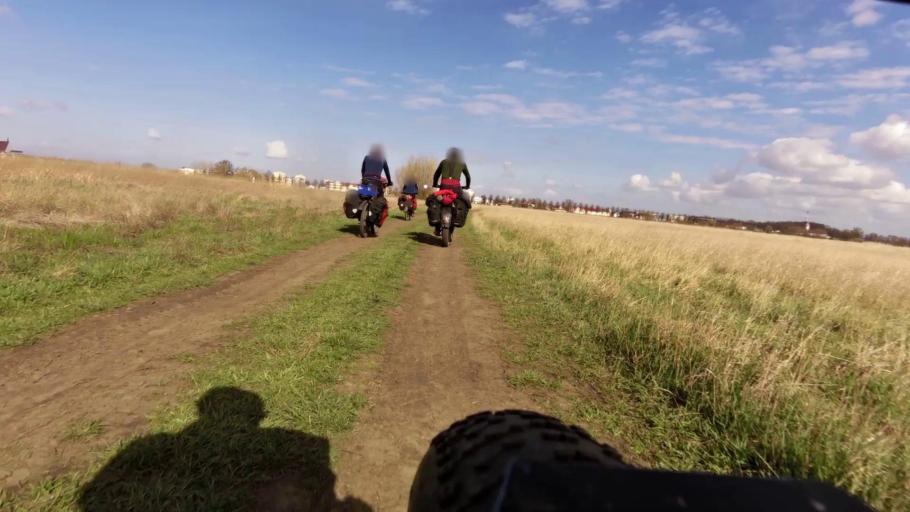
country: PL
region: Lubusz
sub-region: Powiat slubicki
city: Slubice
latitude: 52.3413
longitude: 14.5642
